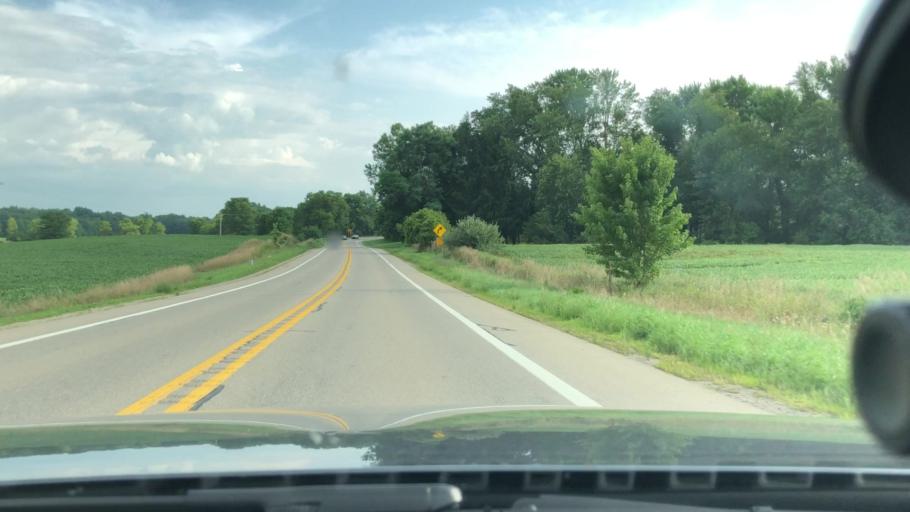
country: US
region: Michigan
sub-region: Washtenaw County
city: Manchester
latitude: 42.1687
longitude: -84.0318
